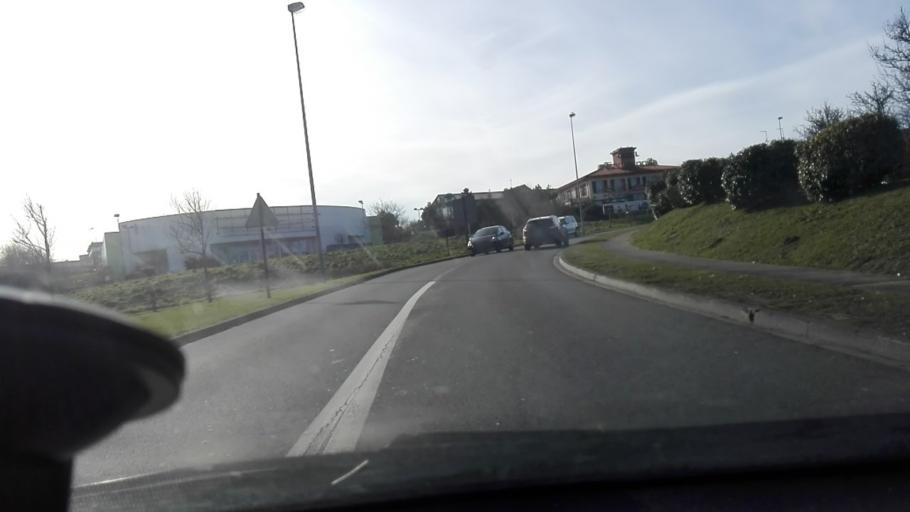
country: FR
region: Nord-Pas-de-Calais
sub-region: Departement du Pas-de-Calais
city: Saint-Martin-Boulogne
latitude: 50.7273
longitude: 1.6433
